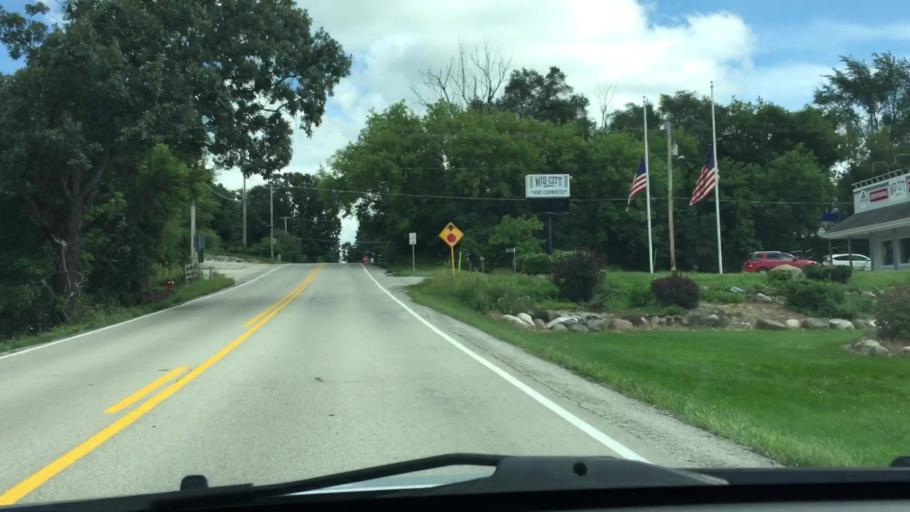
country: US
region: Wisconsin
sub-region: Waukesha County
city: Hartland
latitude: 43.1197
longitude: -88.3328
